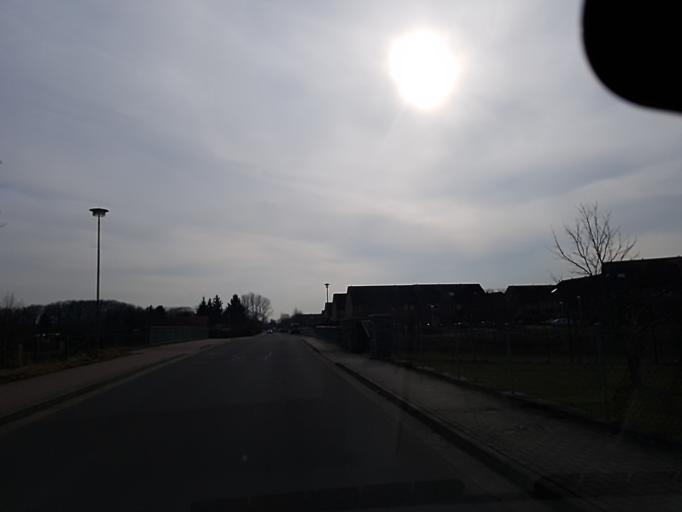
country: DE
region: Brandenburg
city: Doberlug-Kirchhain
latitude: 51.6294
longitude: 13.5574
